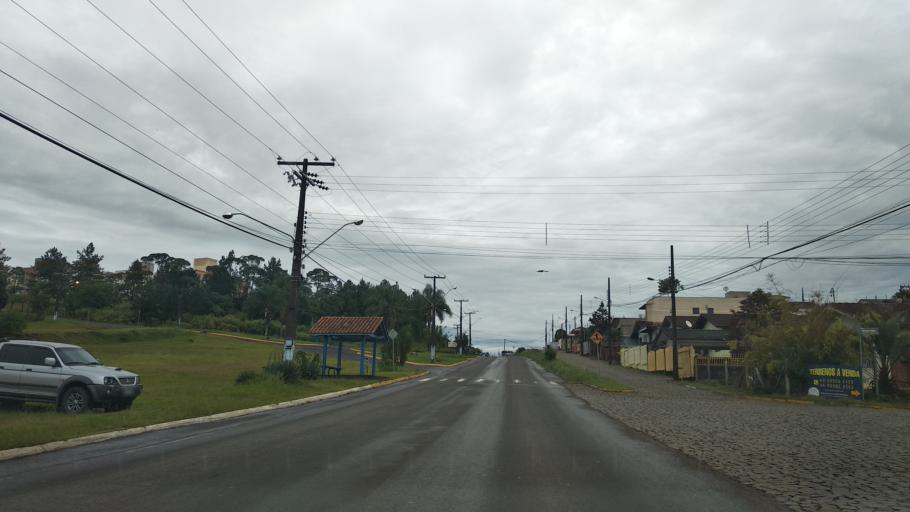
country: BR
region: Santa Catarina
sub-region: Videira
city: Videira
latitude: -26.9924
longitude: -51.1815
